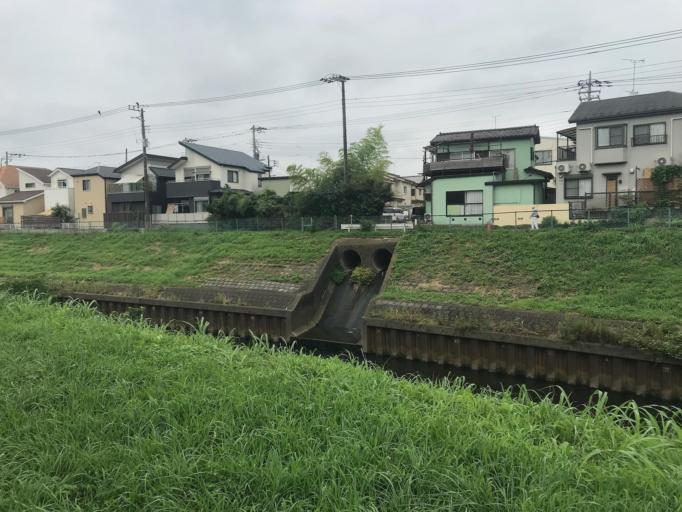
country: JP
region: Saitama
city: Asaka
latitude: 35.7839
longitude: 139.5783
